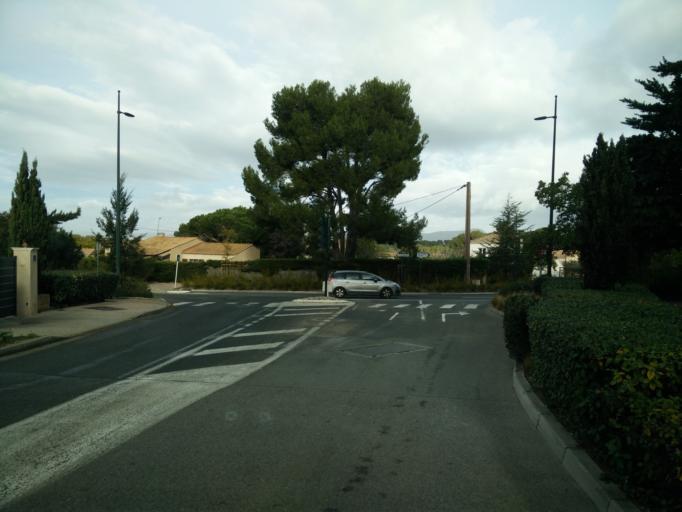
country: FR
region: Provence-Alpes-Cote d'Azur
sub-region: Departement du Var
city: Six-Fours-les-Plages
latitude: 43.0759
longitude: 5.8153
